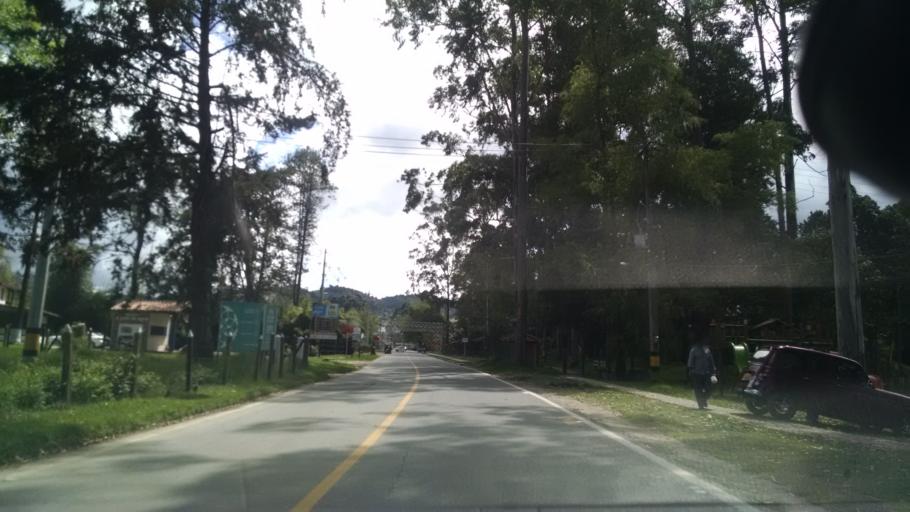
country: CO
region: Antioquia
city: El Retiro
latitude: 6.0700
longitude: -75.4998
